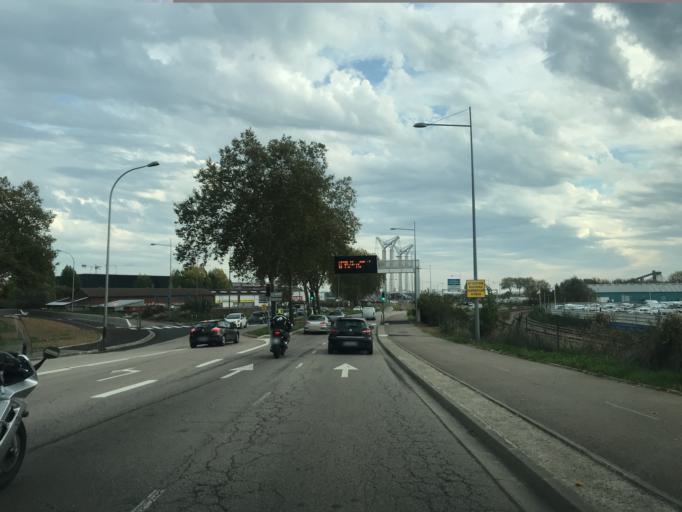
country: FR
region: Haute-Normandie
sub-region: Departement de la Seine-Maritime
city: Deville-les-Rouen
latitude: 49.4499
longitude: 1.0586
